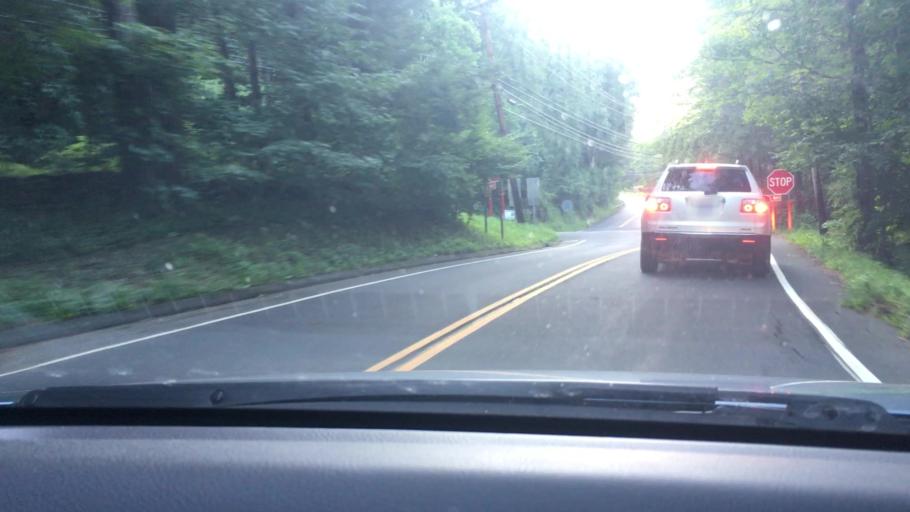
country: US
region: Connecticut
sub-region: Fairfield County
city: Georgetown
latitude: 41.2929
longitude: -73.3943
